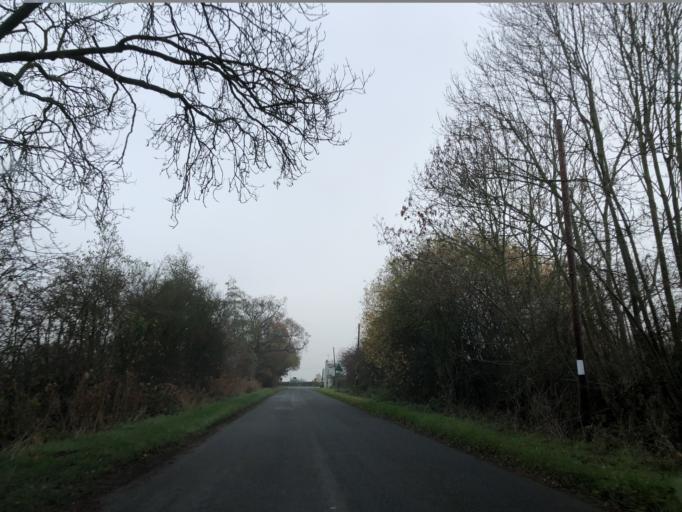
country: GB
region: England
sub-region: Solihull
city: Balsall Common
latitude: 52.3673
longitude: -1.6442
